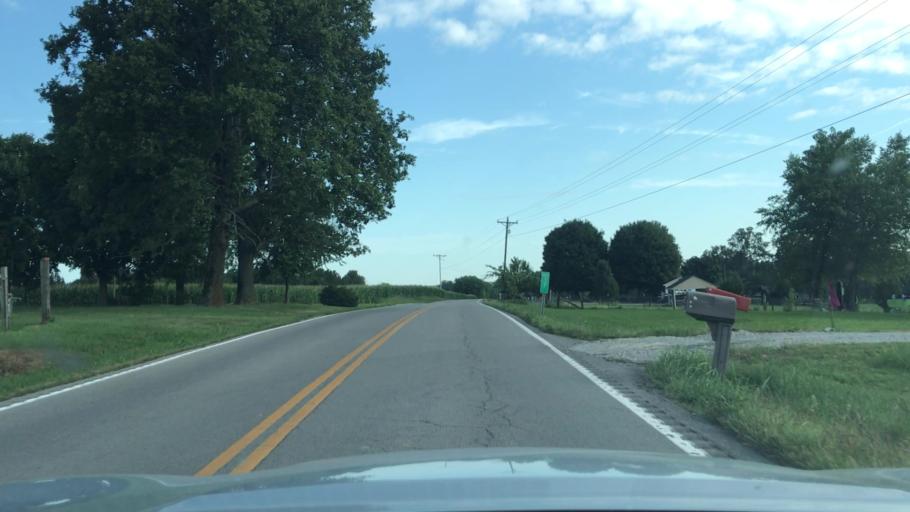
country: US
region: Kentucky
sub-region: Todd County
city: Elkton
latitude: 36.8754
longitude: -87.1665
